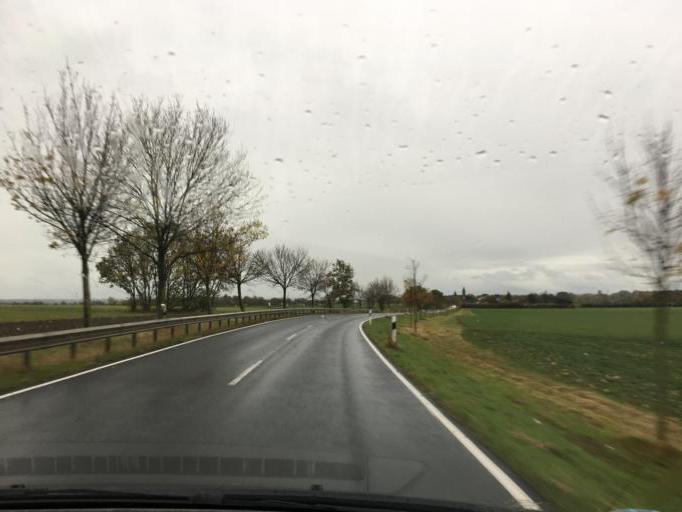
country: DE
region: North Rhine-Westphalia
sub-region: Regierungsbezirk Koln
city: Vettweiss
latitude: 50.7224
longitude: 6.5640
